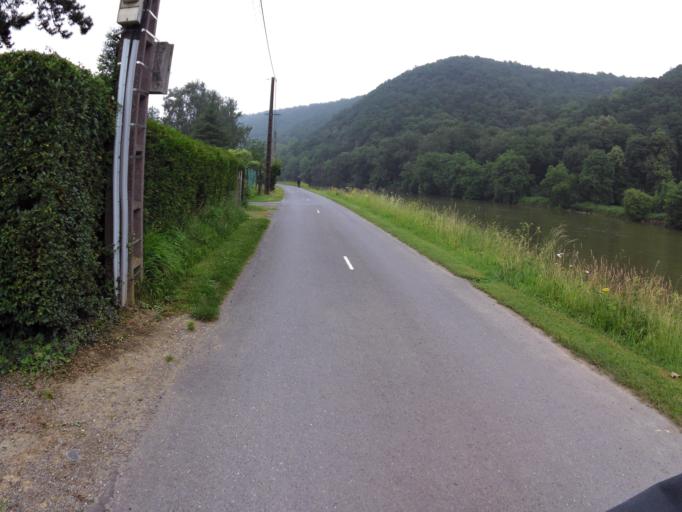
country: FR
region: Champagne-Ardenne
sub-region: Departement des Ardennes
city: Fumay
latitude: 49.9919
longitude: 4.7154
